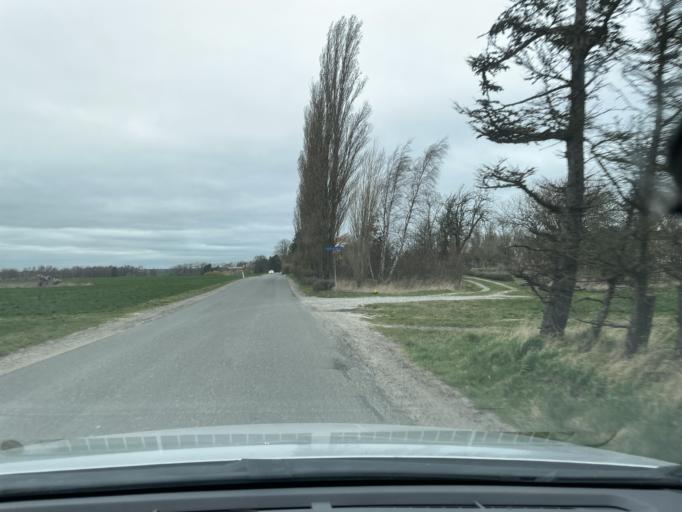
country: DK
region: South Denmark
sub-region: Nyborg Kommune
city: Nyborg
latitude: 55.3526
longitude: 10.7906
